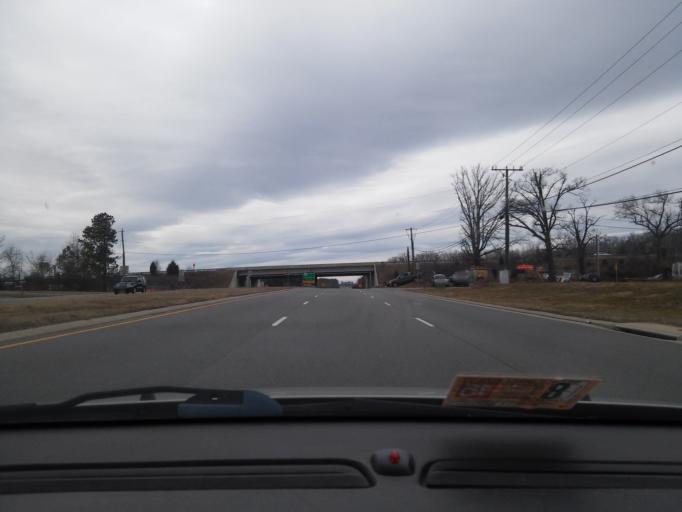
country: US
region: Virginia
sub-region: Henrico County
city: Short Pump
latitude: 37.6638
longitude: -77.6541
